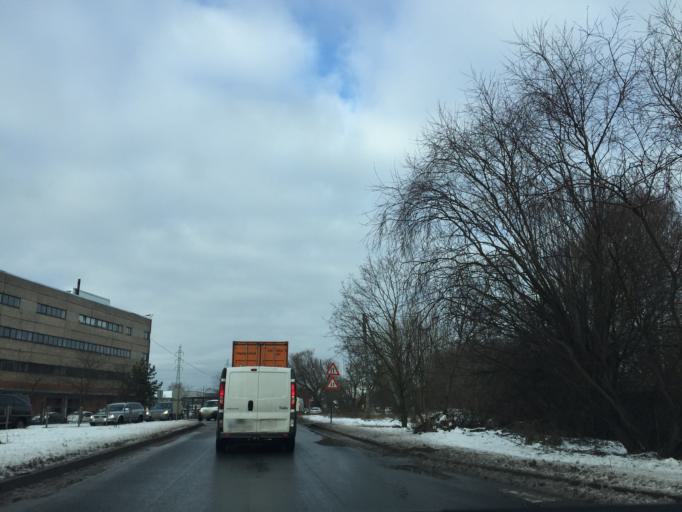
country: LV
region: Riga
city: Riga
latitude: 56.9466
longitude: 24.1645
